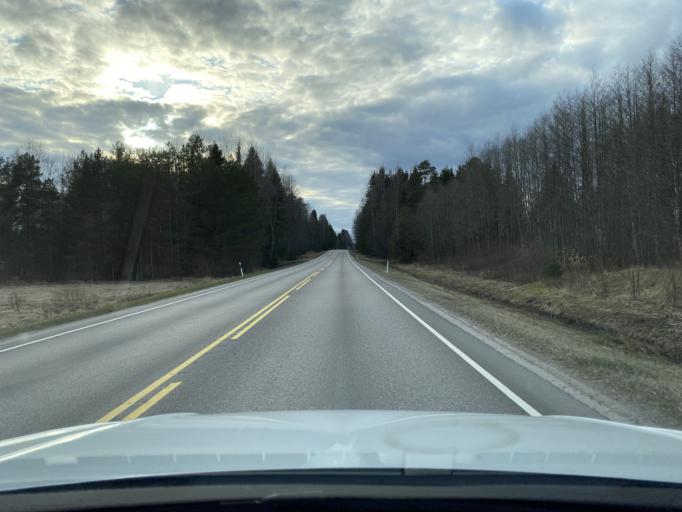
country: FI
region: Haeme
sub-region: Haemeenlinna
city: Renko
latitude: 60.7907
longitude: 24.1212
